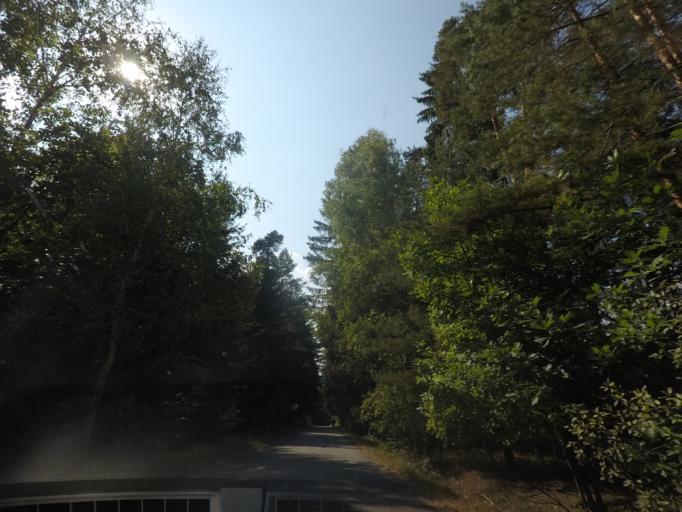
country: CZ
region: Pardubicky
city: Horni Jeleni
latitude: 50.0643
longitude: 16.0763
